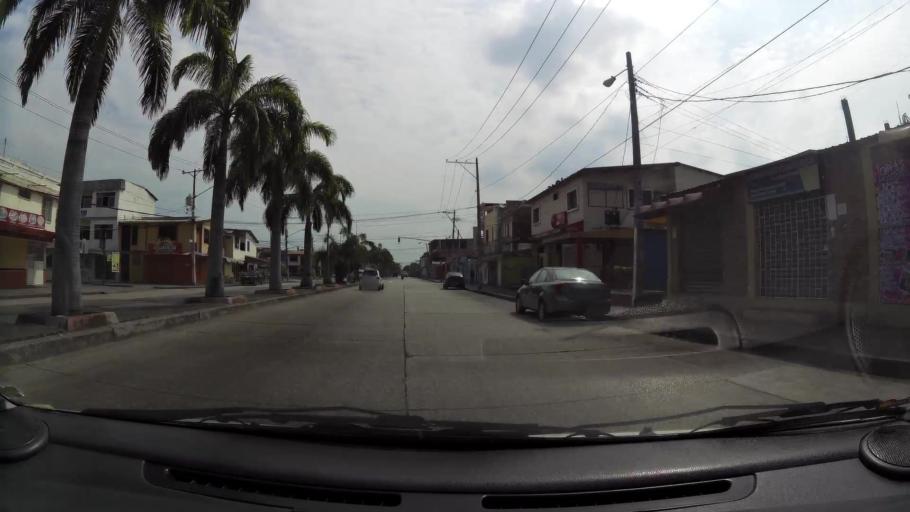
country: EC
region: Guayas
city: Guayaquil
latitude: -2.2413
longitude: -79.8998
